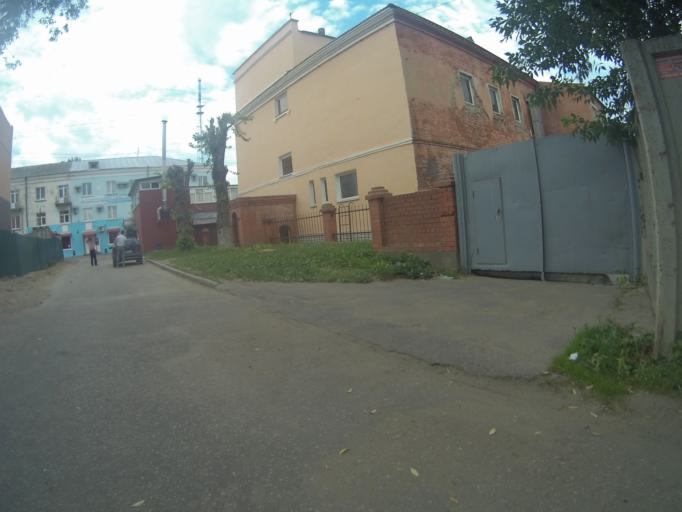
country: RU
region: Vladimir
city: Vladimir
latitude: 56.1398
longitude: 40.3933
